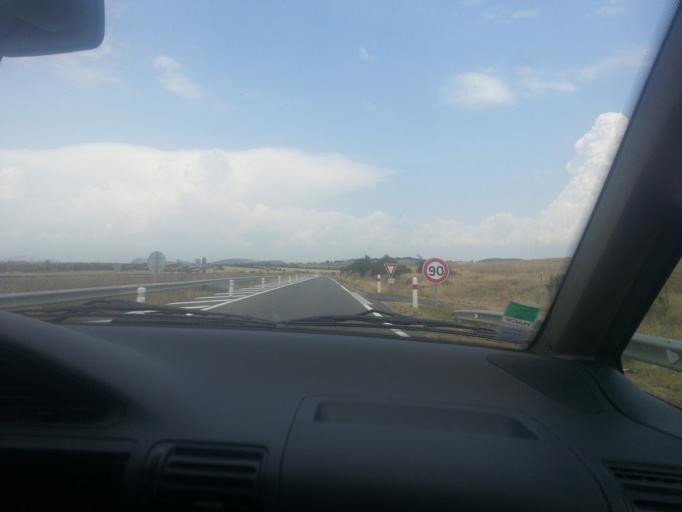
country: FR
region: Midi-Pyrenees
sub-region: Departement de l'Aveyron
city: Millau
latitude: 44.0714
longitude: 3.1135
